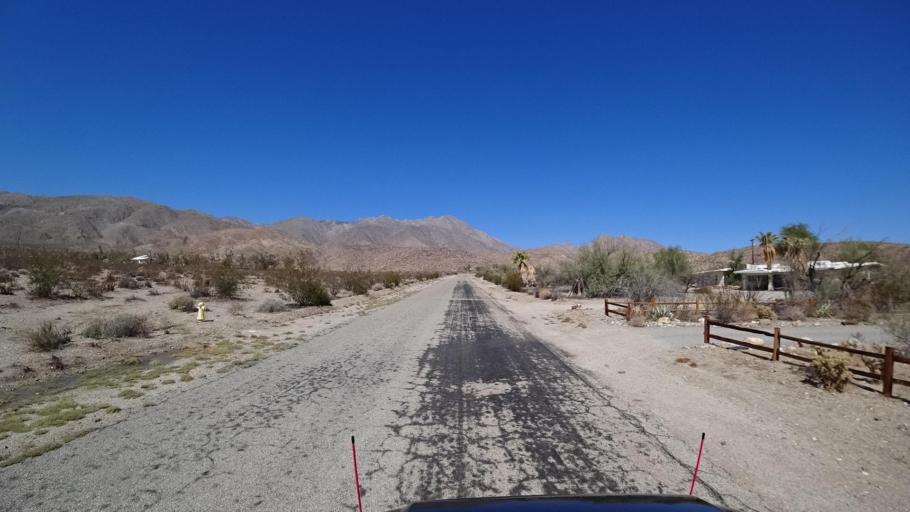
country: US
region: California
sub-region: San Diego County
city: Borrego Springs
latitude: 33.2380
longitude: -116.3847
